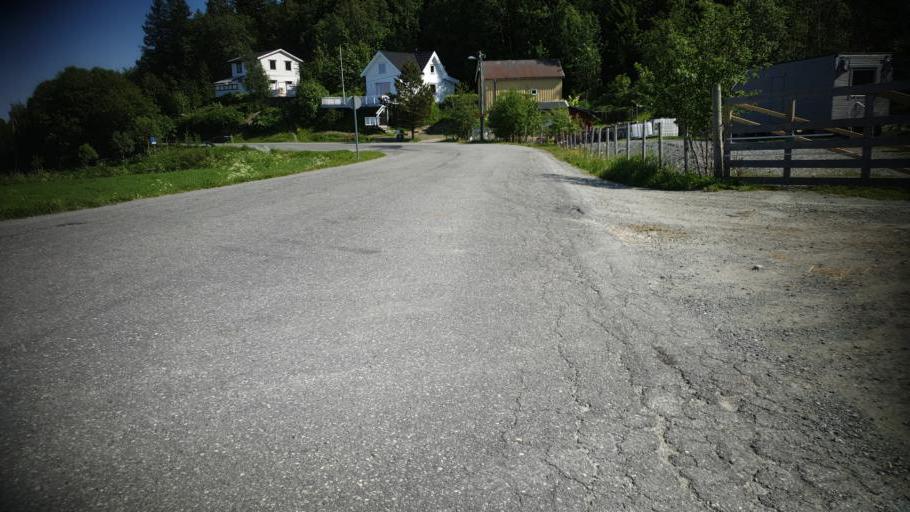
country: NO
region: Sor-Trondelag
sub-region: Malvik
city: Malvik
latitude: 63.4321
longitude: 10.5958
